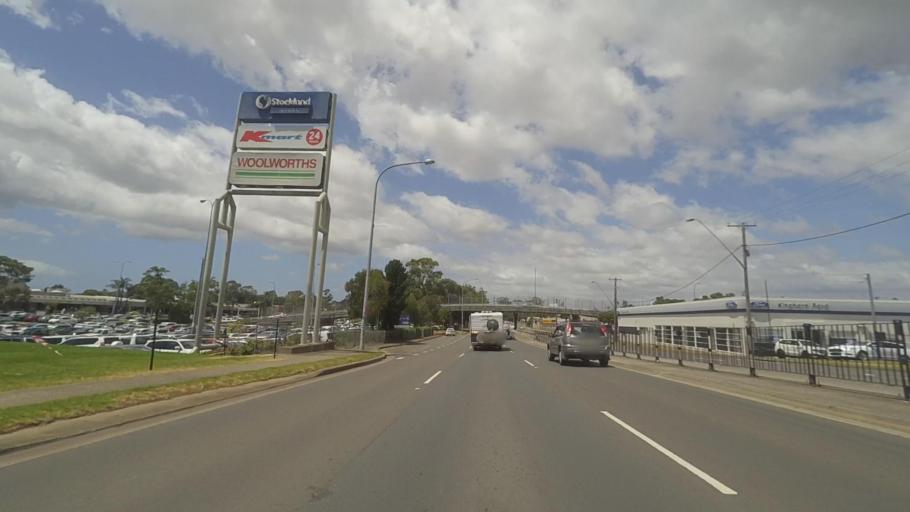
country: AU
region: New South Wales
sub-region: Shoalhaven Shire
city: Nowra
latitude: -34.8752
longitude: 150.6055
